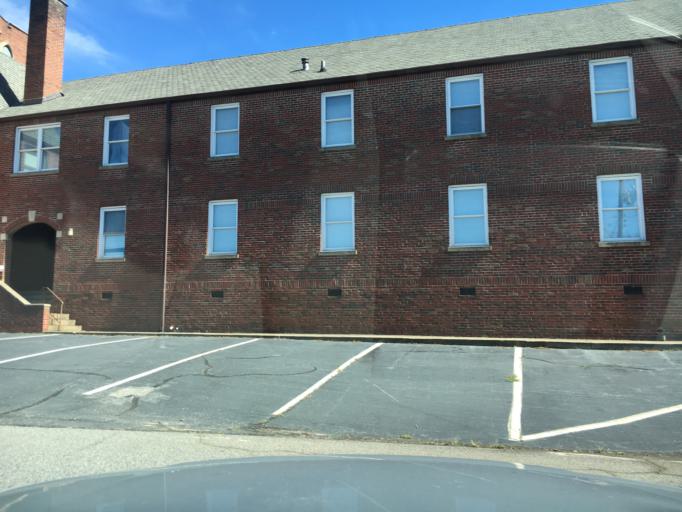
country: US
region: South Carolina
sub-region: Spartanburg County
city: Duncan
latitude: 34.9360
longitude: -82.1369
